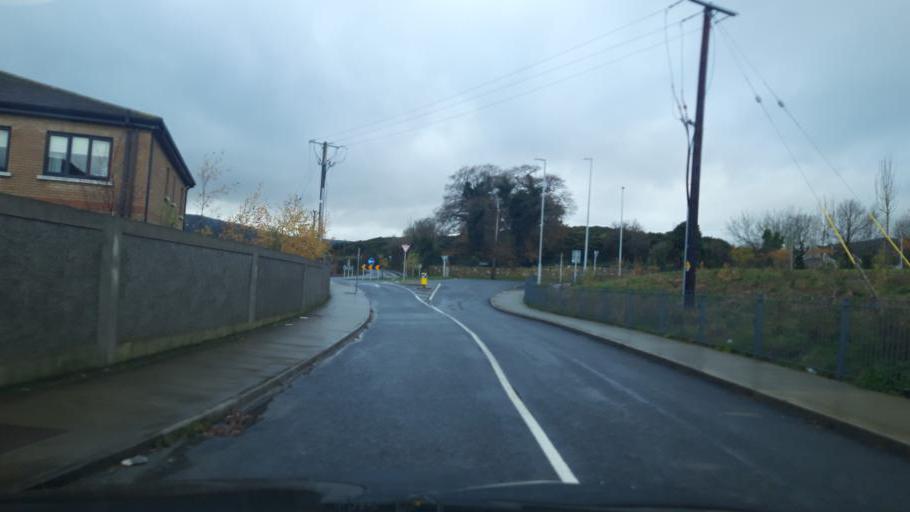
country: IE
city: Newtownmountkennedy
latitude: 53.0857
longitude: -6.1149
